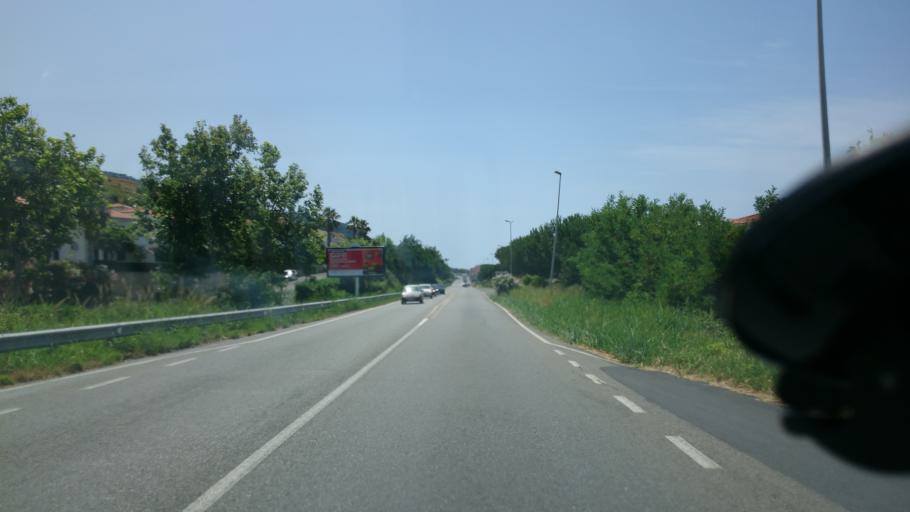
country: IT
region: Calabria
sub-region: Provincia di Cosenza
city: Cittadella del Capo
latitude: 39.5750
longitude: 15.8710
